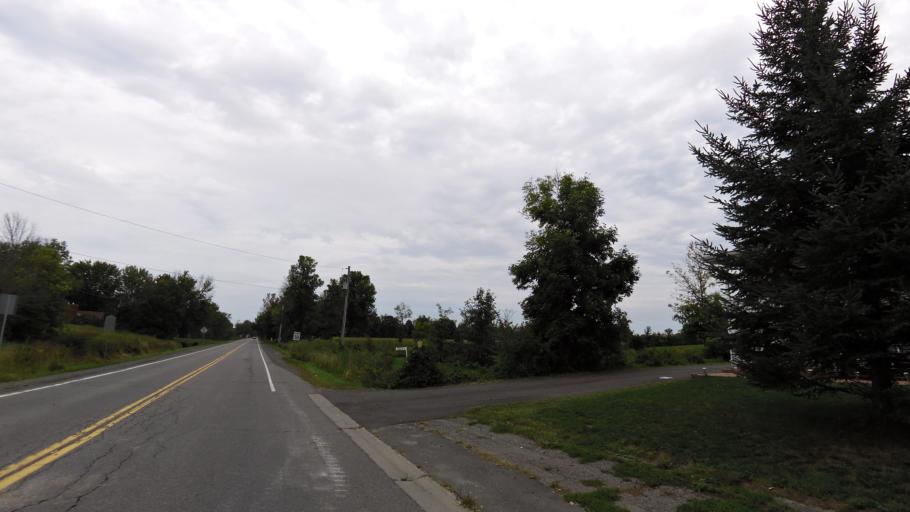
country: CA
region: Ontario
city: Ottawa
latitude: 45.2366
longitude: -75.4732
